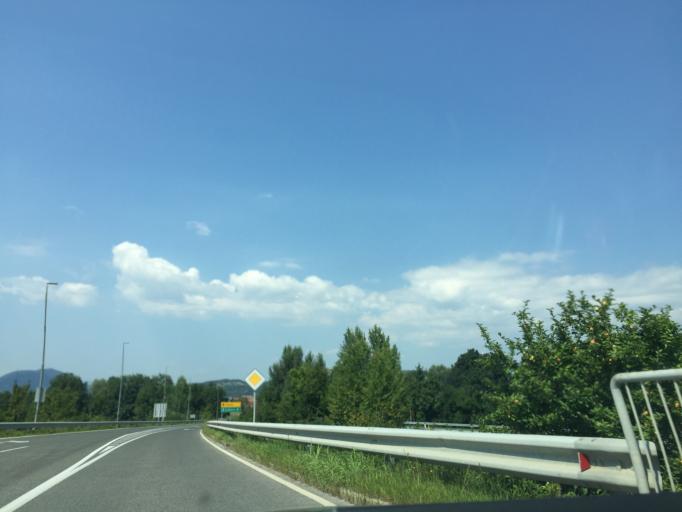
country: SI
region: Zalec
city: Sempeter v Savinj. Dolini
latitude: 46.2600
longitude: 15.0990
